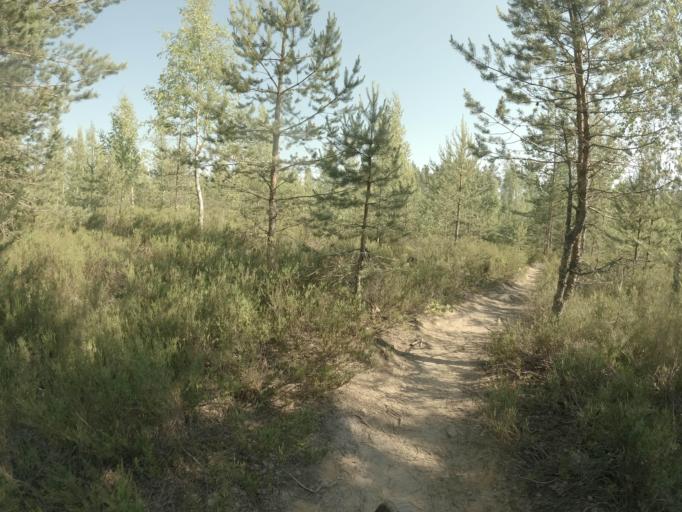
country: RU
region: Leningrad
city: Yakovlevo
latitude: 60.4391
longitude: 29.2391
